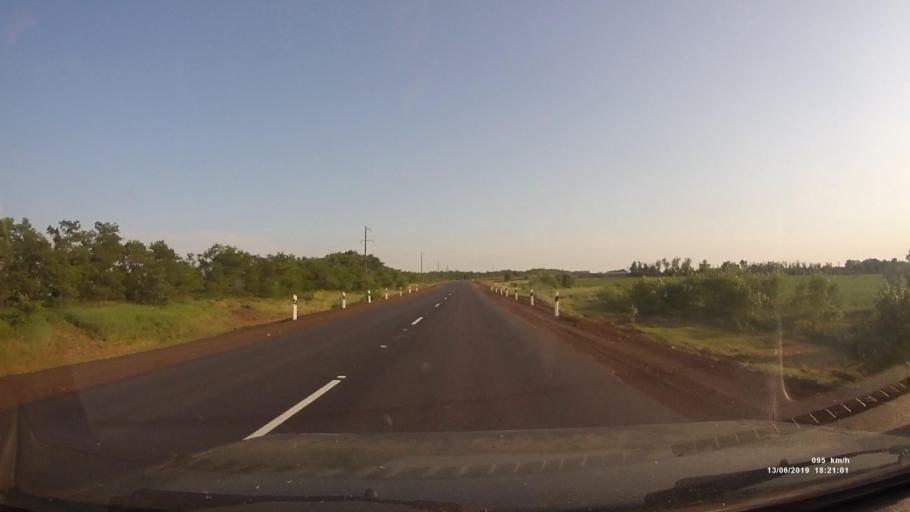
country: RU
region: Rostov
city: Kazanskaya
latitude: 49.8761
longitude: 41.2947
